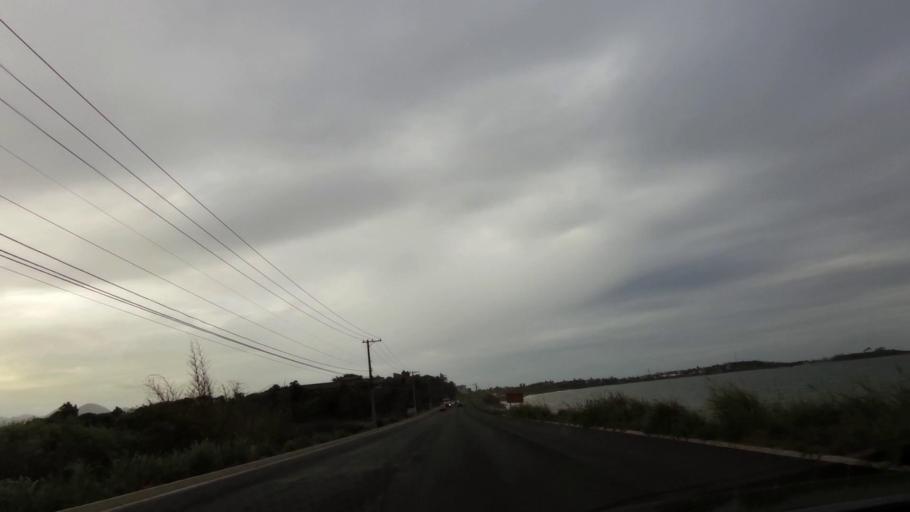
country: BR
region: Espirito Santo
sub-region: Guarapari
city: Guarapari
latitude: -20.7503
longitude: -40.5604
